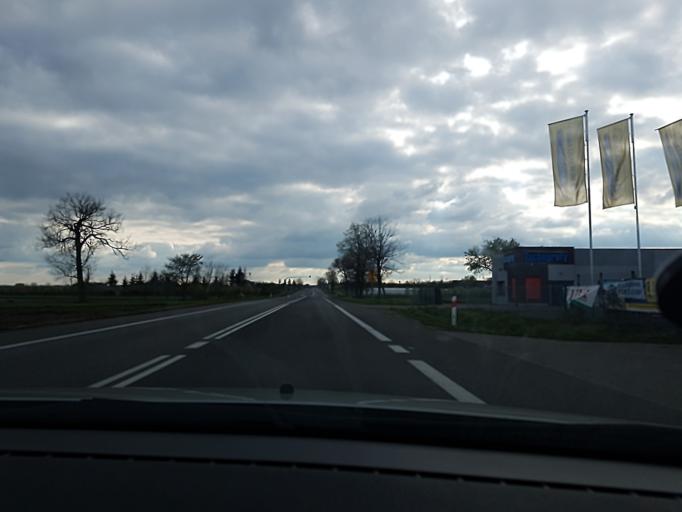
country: PL
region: Lodz Voivodeship
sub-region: powiat Lowicki
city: Lowicz
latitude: 52.1217
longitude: 19.9947
